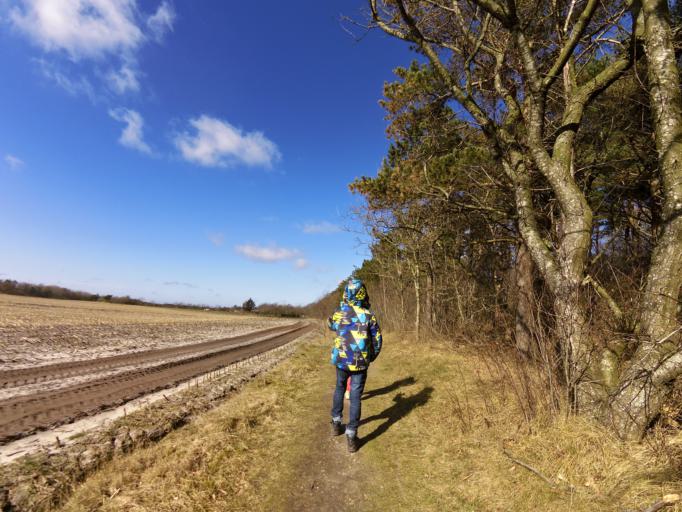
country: DK
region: South Denmark
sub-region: Varde Kommune
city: Varde
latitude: 55.5842
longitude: 8.4115
